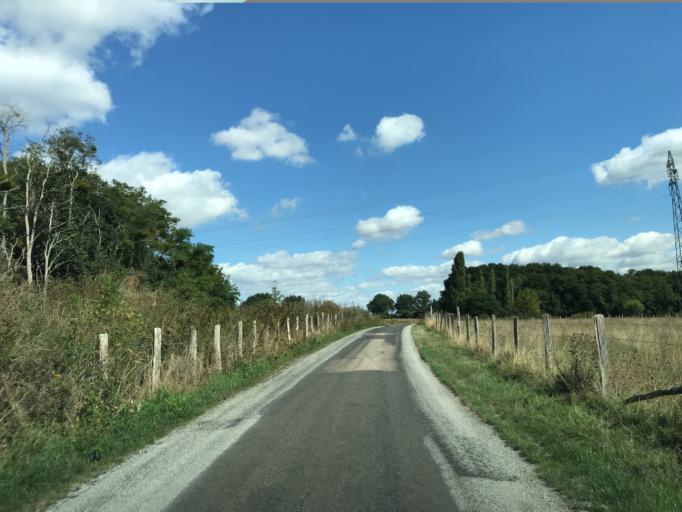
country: FR
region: Haute-Normandie
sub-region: Departement de l'Eure
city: La Chapelle-Reanville
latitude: 49.1204
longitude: 1.3812
